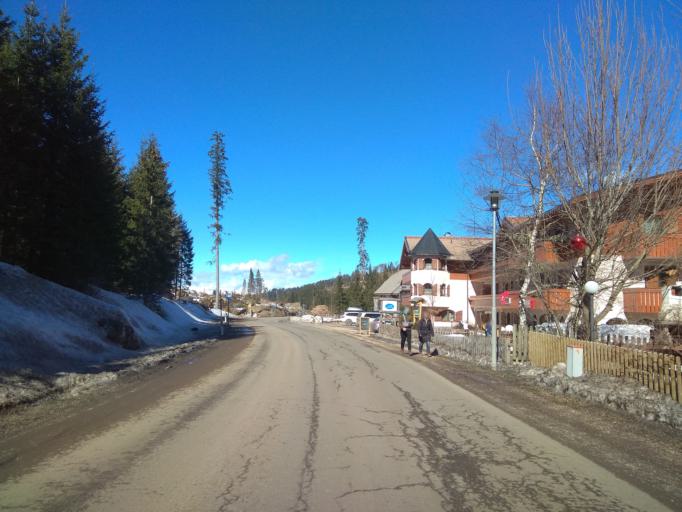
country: IT
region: Trentino-Alto Adige
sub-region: Bolzano
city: Nova Levante
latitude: 46.4078
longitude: 11.5827
